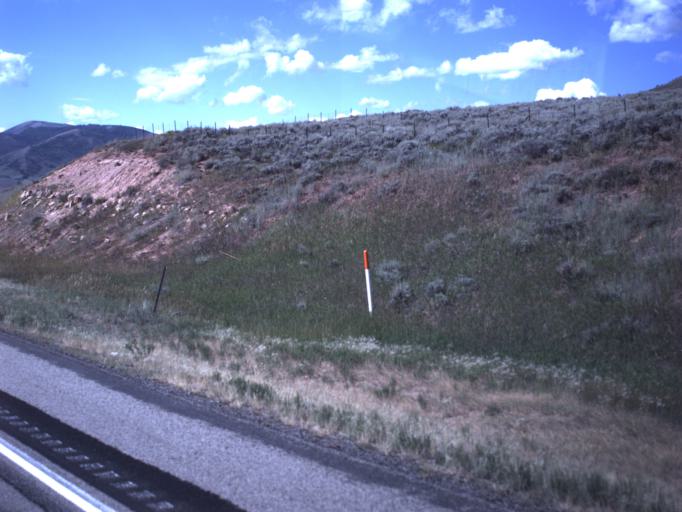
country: US
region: Utah
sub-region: Wasatch County
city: Heber
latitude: 40.1993
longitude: -111.1040
